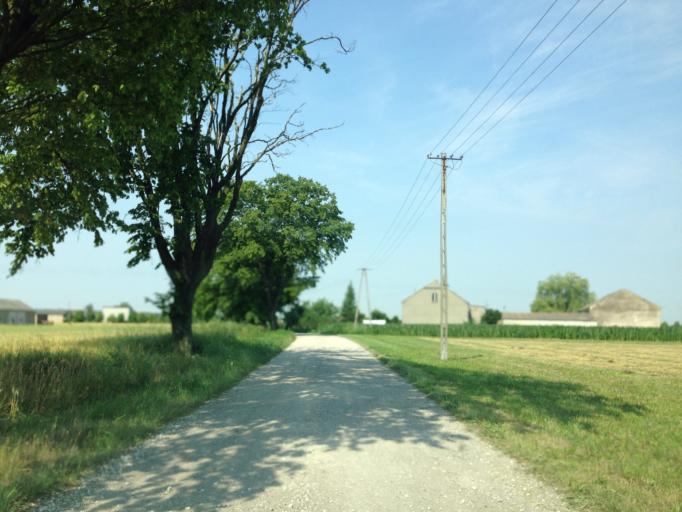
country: PL
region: Kujawsko-Pomorskie
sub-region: Powiat rypinski
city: Wapielsk
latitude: 53.2030
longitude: 19.2419
